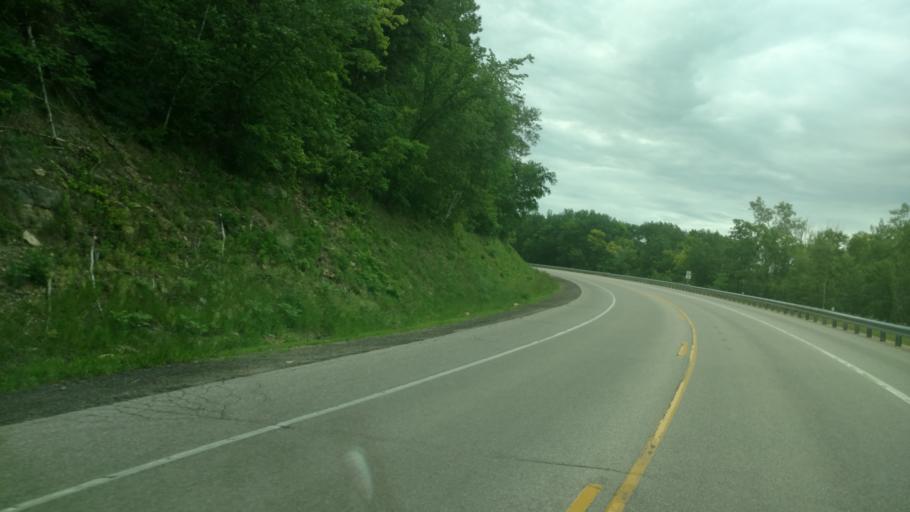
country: US
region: Wisconsin
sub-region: Monroe County
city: Tomah
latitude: 43.8157
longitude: -90.4358
